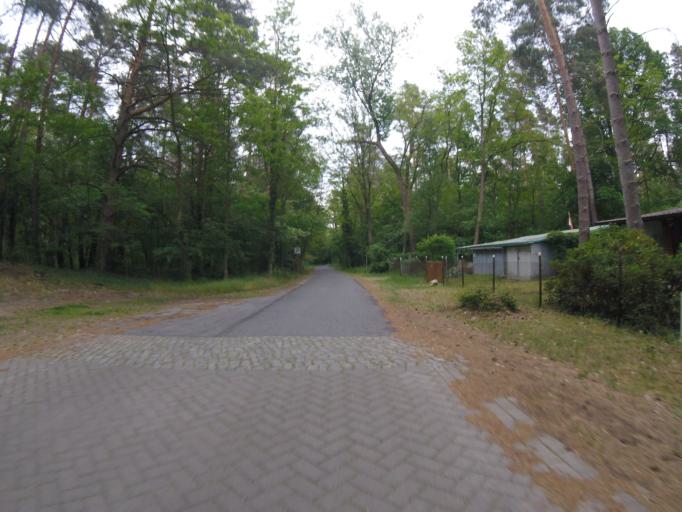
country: DE
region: Brandenburg
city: Bestensee
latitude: 52.2257
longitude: 13.6717
